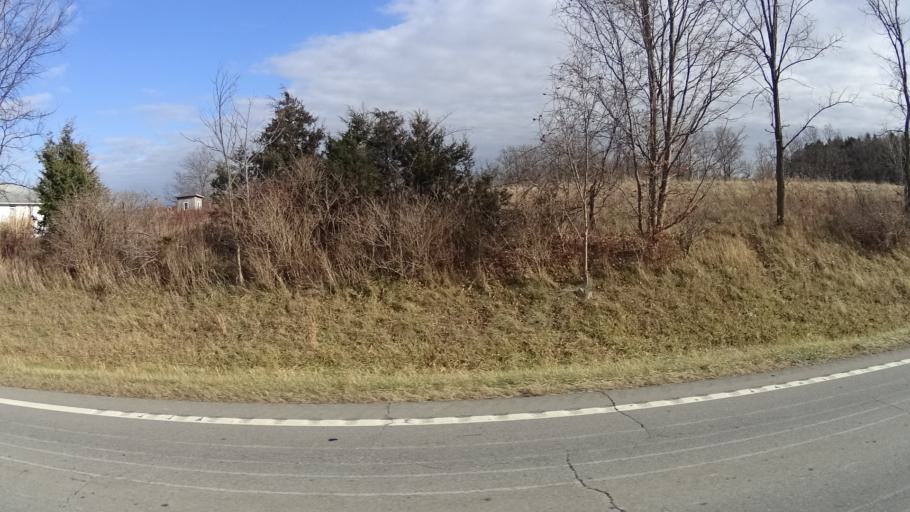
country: US
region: Ohio
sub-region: Lorain County
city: Camden
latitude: 41.1501
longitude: -82.3105
